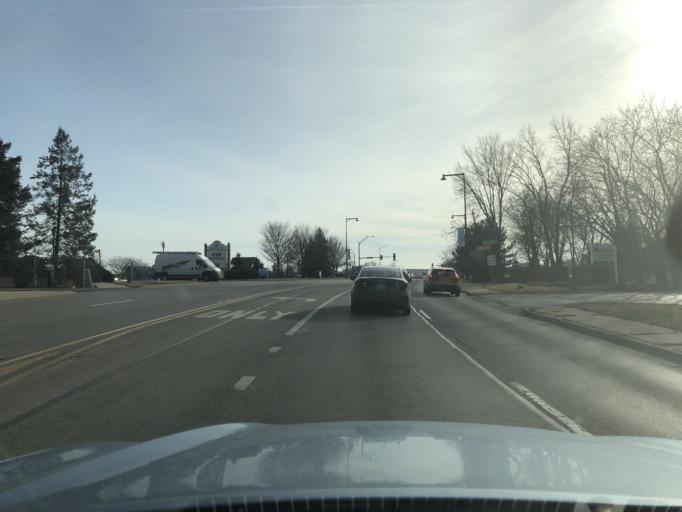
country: US
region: Illinois
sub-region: DuPage County
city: Bloomingdale
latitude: 41.9595
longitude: -88.0814
